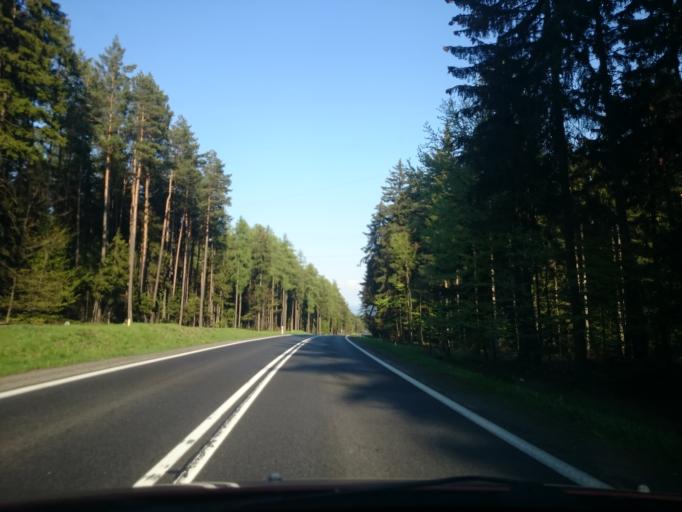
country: PL
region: Lower Silesian Voivodeship
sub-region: Powiat klodzki
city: Szczytna
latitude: 50.4258
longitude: 16.4789
